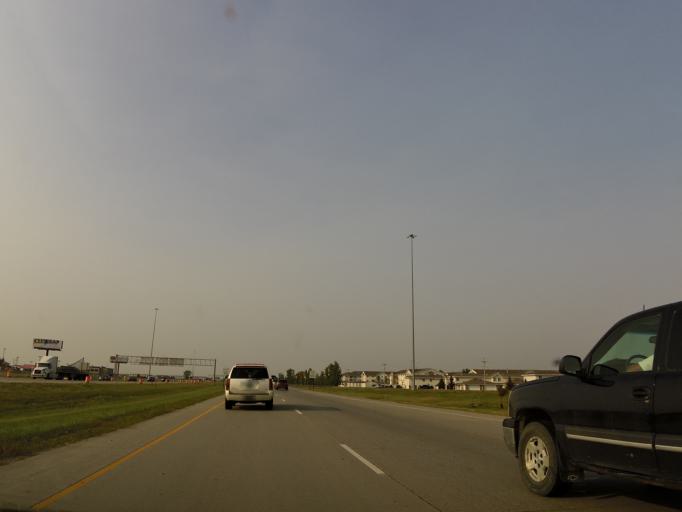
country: US
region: North Dakota
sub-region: Cass County
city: Fargo
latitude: 46.8345
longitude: -96.8400
